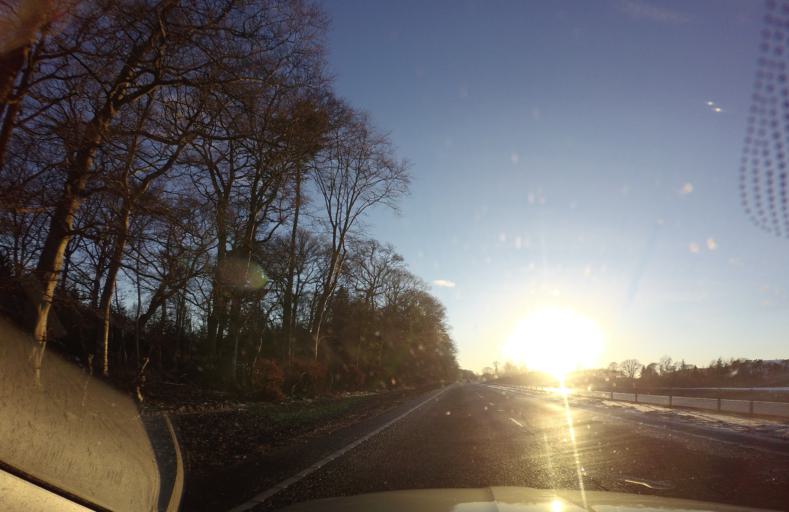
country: GB
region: Scotland
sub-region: Perth and Kinross
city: Errol
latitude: 56.4122
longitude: -3.2401
